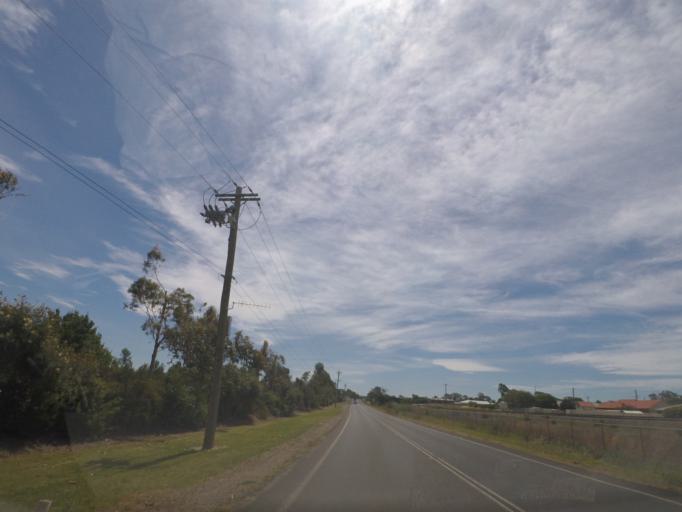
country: AU
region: New South Wales
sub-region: Wollondilly
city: Buxton
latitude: -34.2977
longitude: 150.5855
